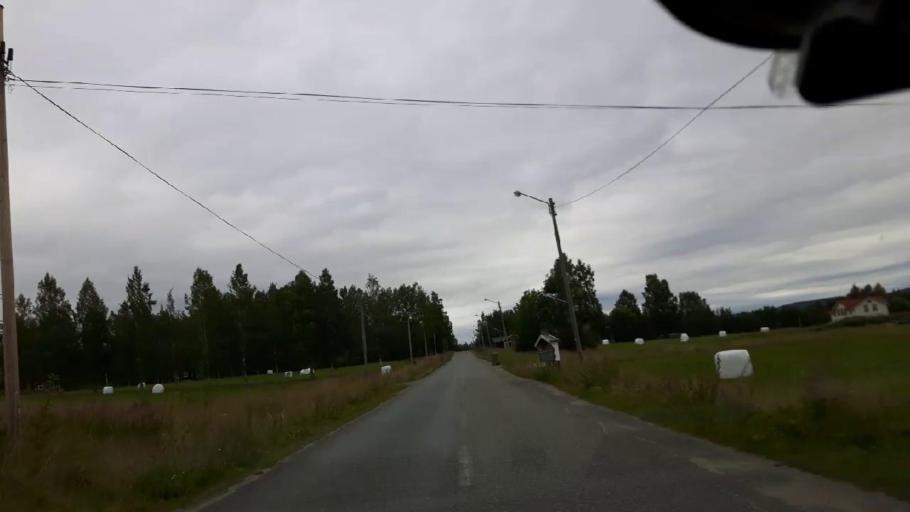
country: SE
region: Jaemtland
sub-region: Braecke Kommun
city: Braecke
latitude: 62.8404
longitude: 15.6794
